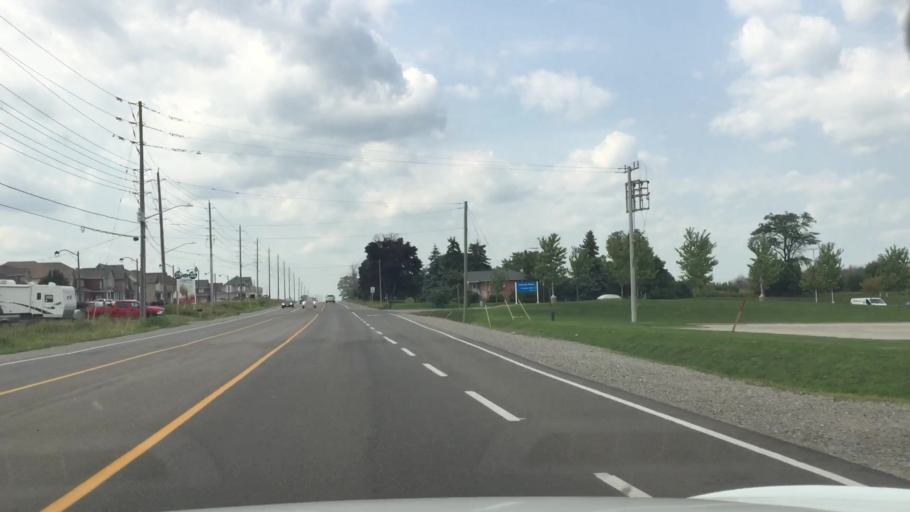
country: CA
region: Ontario
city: Oshawa
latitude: 43.9479
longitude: -78.8531
